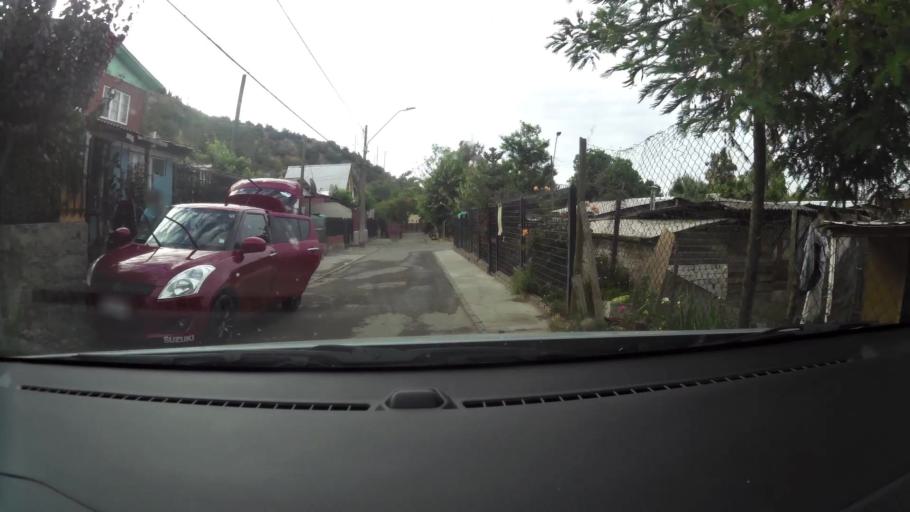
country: CL
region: Santiago Metropolitan
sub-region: Provincia de Maipo
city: San Bernardo
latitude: -33.6472
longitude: -70.6665
